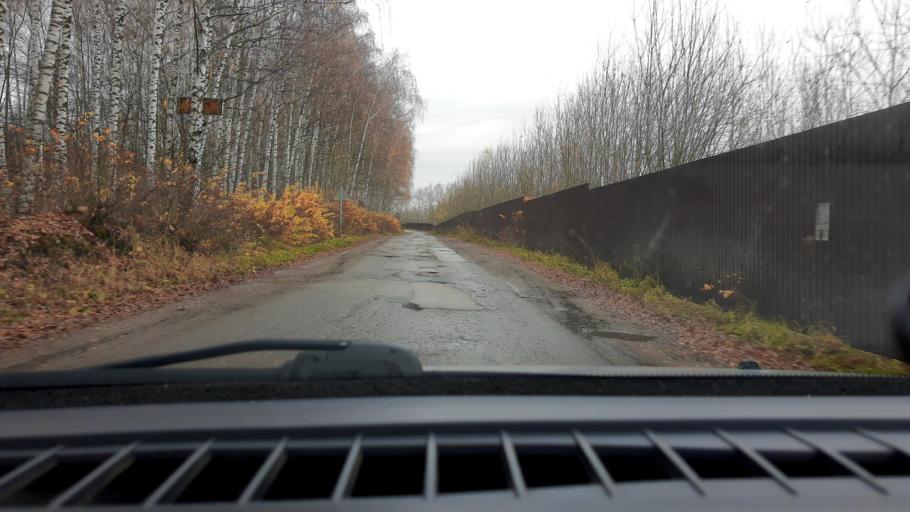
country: RU
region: Nizjnij Novgorod
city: Afonino
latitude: 56.1908
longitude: 44.1102
